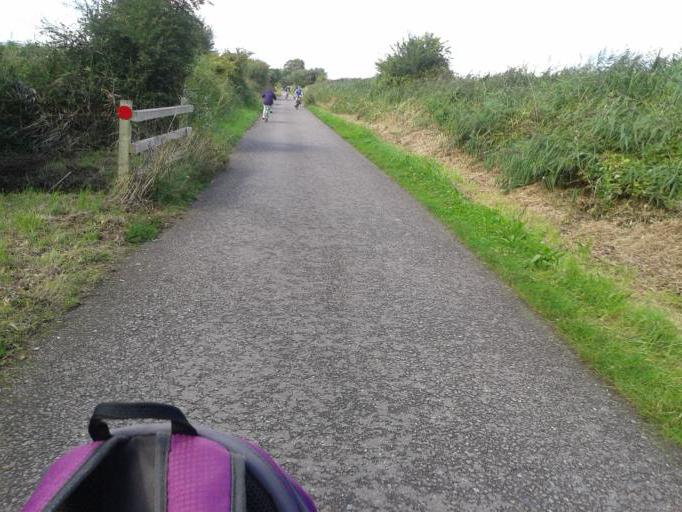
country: GB
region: England
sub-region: Devon
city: Topsham
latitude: 50.6698
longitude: -3.4687
